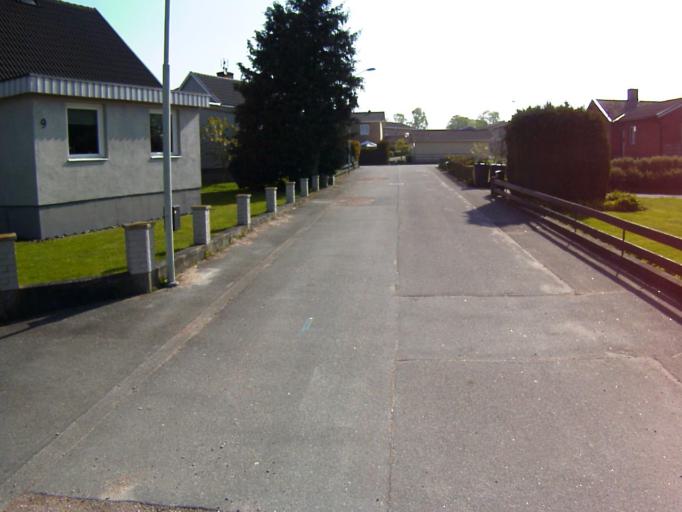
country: SE
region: Skane
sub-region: Kristianstads Kommun
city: Kristianstad
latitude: 56.0311
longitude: 14.2106
